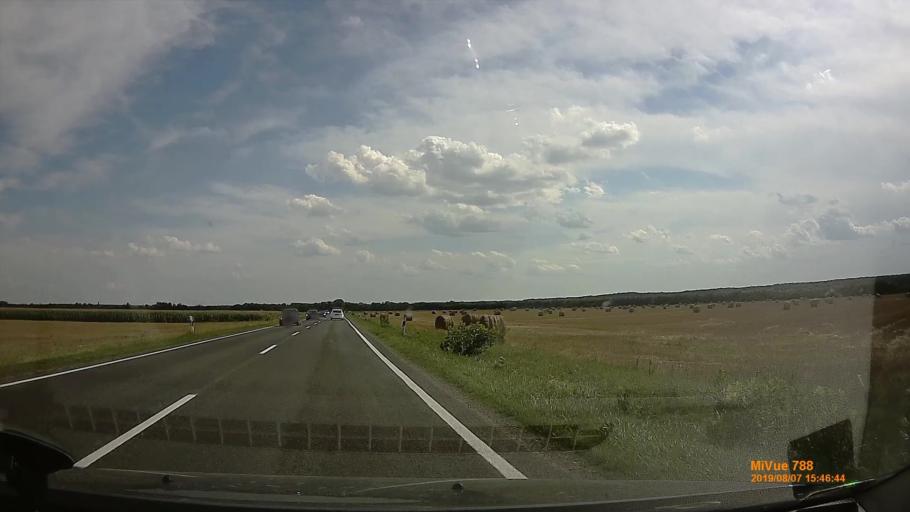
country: HU
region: Vas
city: Szombathely
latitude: 47.1814
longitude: 16.6225
